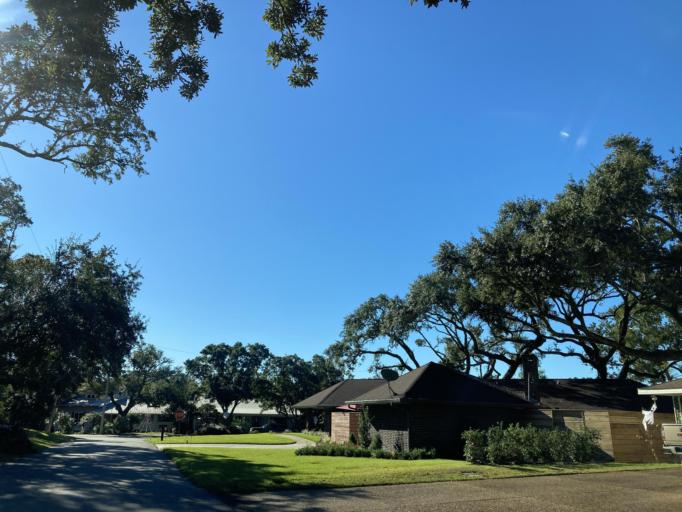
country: US
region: Mississippi
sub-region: Jackson County
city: Ocean Springs
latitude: 30.4173
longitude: -88.8363
